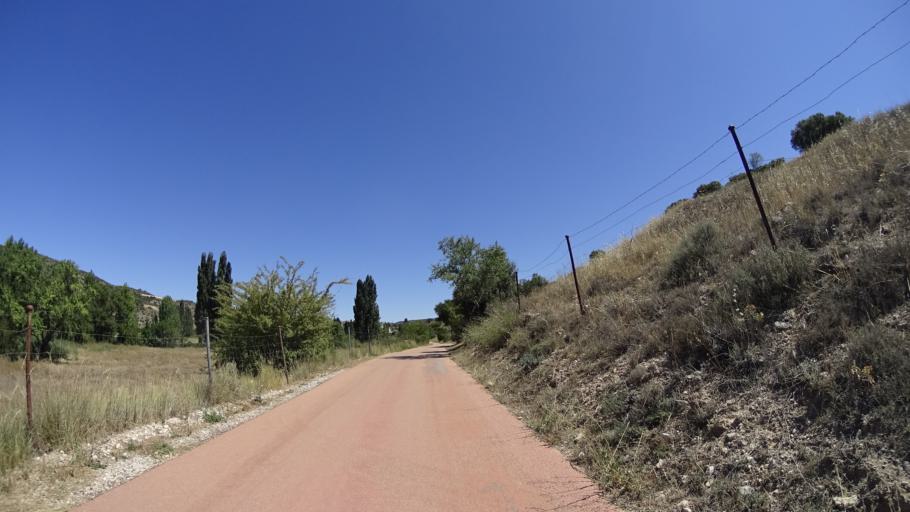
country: ES
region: Madrid
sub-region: Provincia de Madrid
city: Carabana
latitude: 40.2716
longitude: -3.2167
